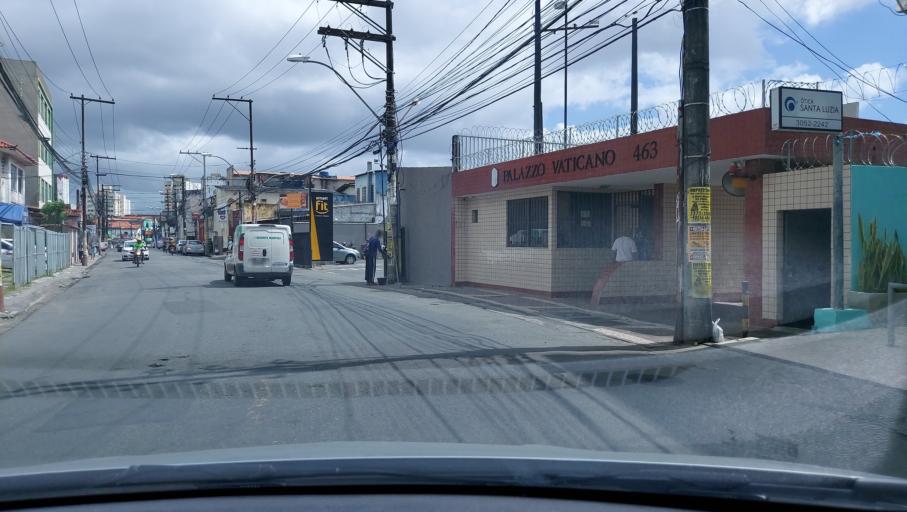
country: BR
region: Bahia
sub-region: Salvador
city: Salvador
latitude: -12.9772
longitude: -38.4951
